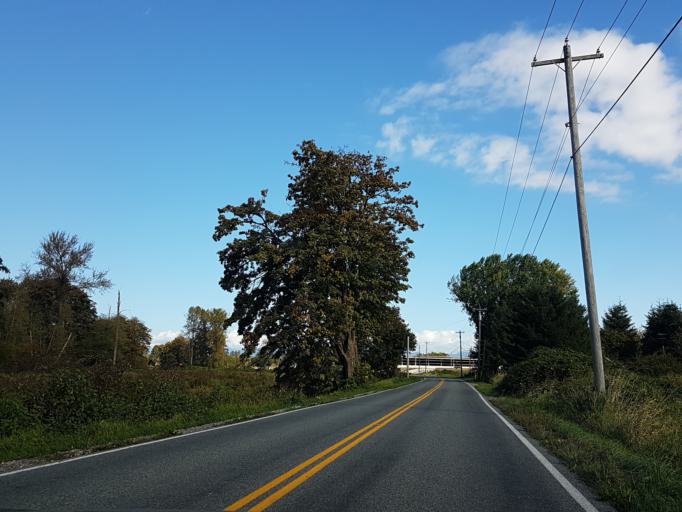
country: US
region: Washington
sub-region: Snohomish County
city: Monroe
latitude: 47.8098
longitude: -121.9922
